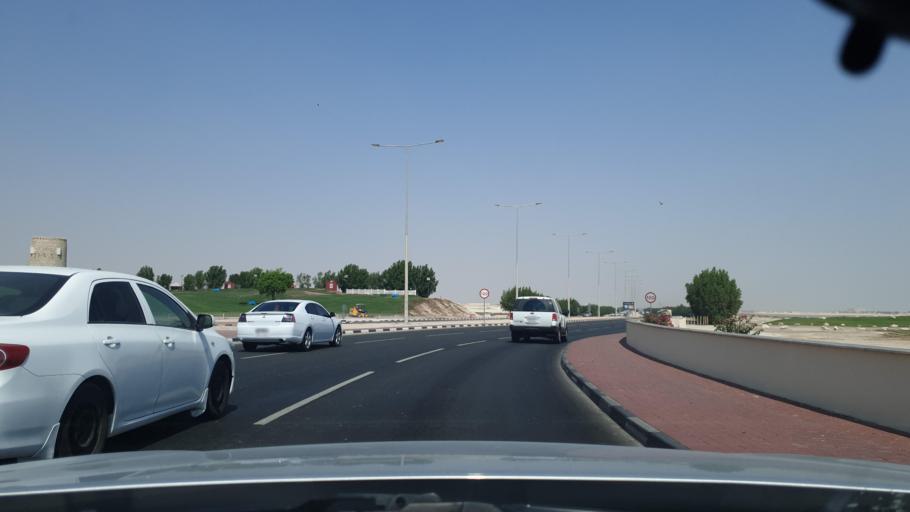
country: QA
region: Al Khawr
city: Al Khawr
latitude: 25.6910
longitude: 51.5004
